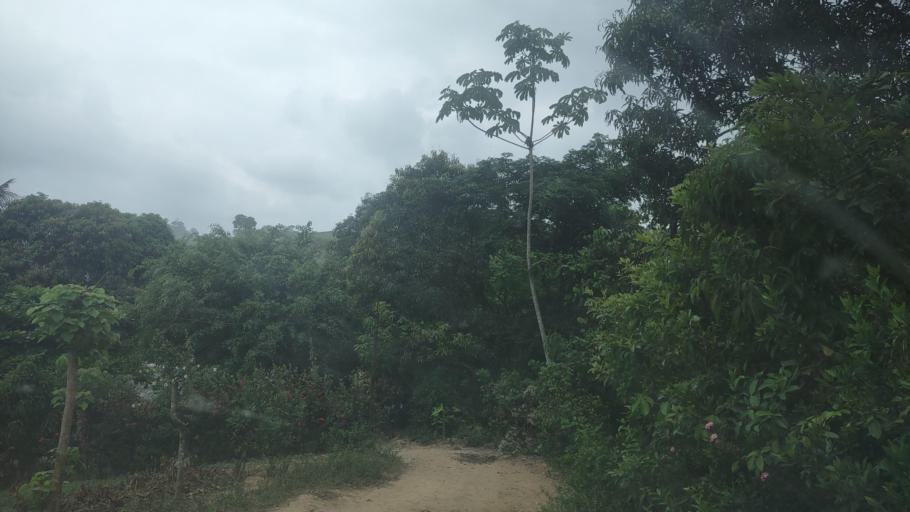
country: MX
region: Tabasco
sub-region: Huimanguillo
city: Francisco Rueda
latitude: 17.4457
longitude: -94.0248
